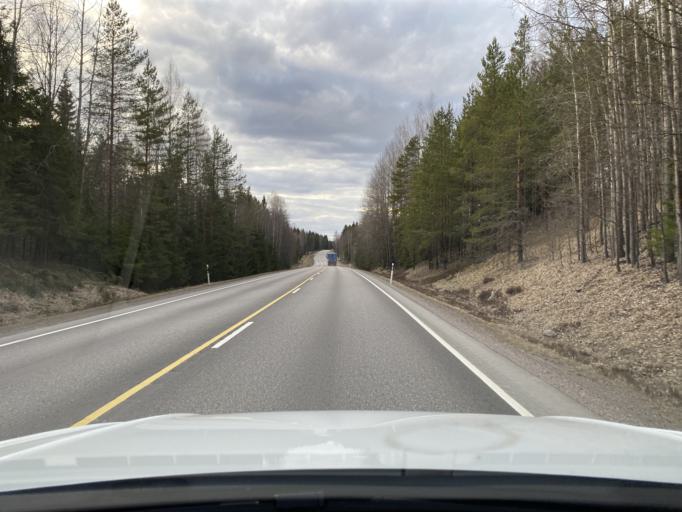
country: FI
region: Haeme
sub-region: Haemeenlinna
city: Renko
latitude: 60.8019
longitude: 24.0795
